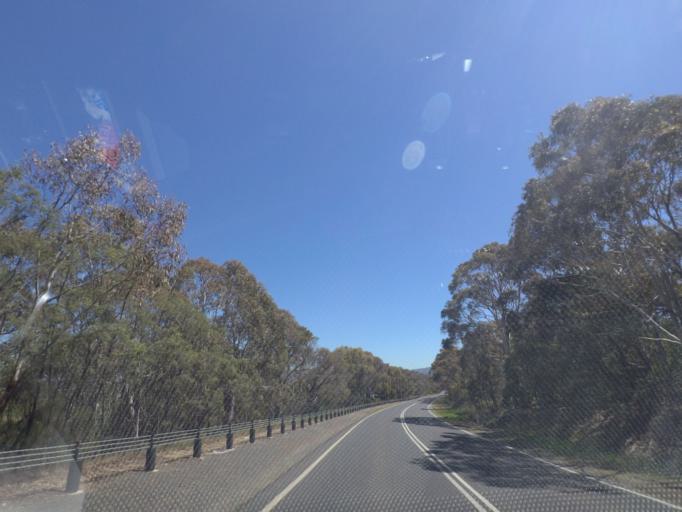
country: AU
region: Victoria
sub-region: Hume
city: Sunbury
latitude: -37.2904
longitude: 144.7901
